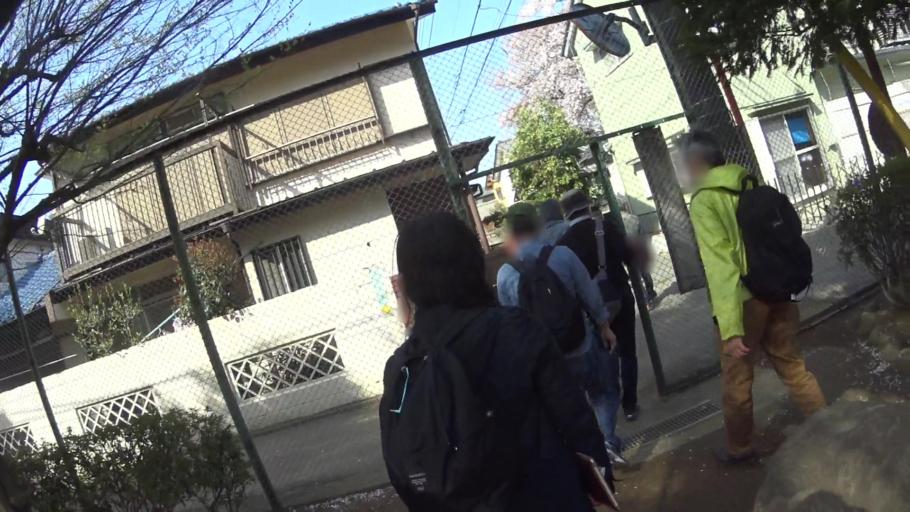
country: JP
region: Tokyo
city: Kokubunji
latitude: 35.7119
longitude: 139.4906
